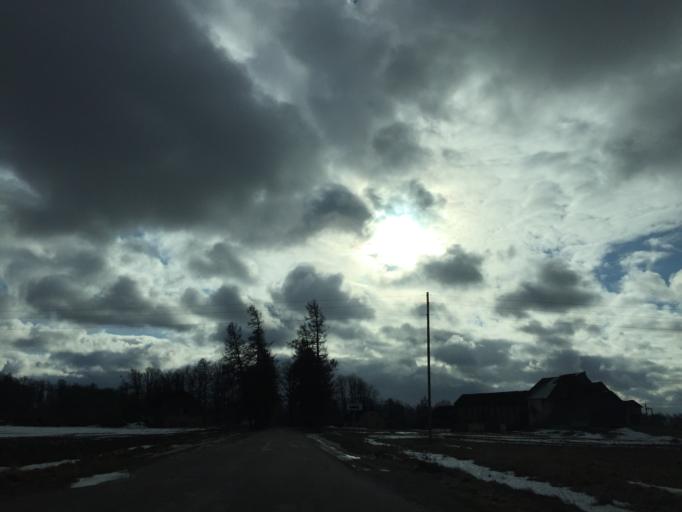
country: LV
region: Aloja
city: Aloja
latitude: 57.7772
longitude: 24.8125
